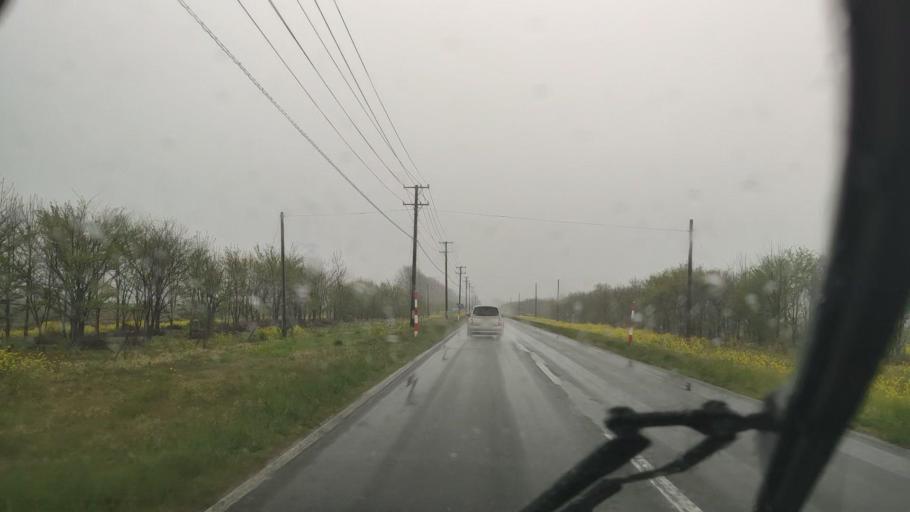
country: JP
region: Akita
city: Tenno
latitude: 39.9656
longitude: 139.9462
